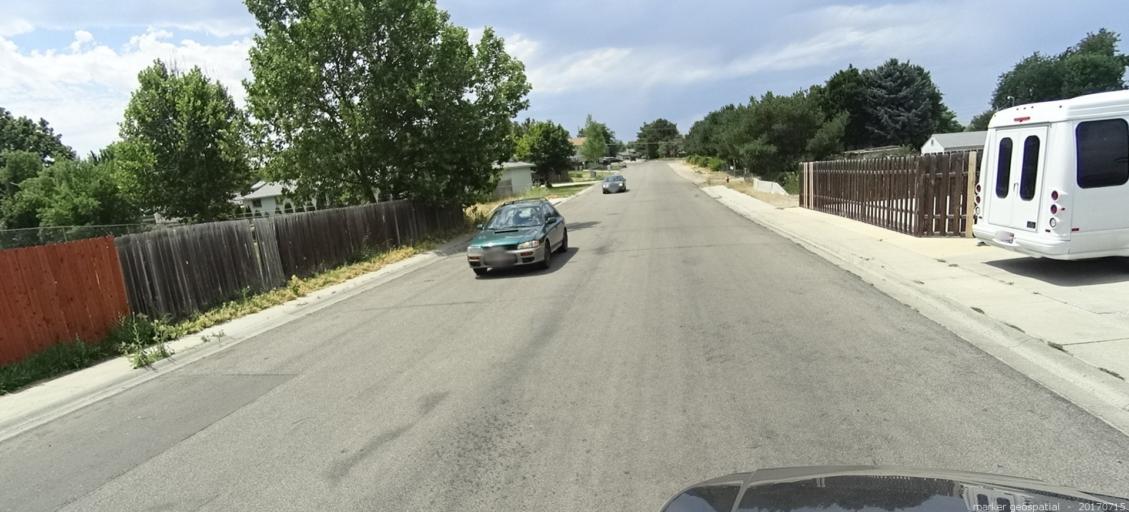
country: US
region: Idaho
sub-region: Ada County
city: Meridian
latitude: 43.5697
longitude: -116.3123
